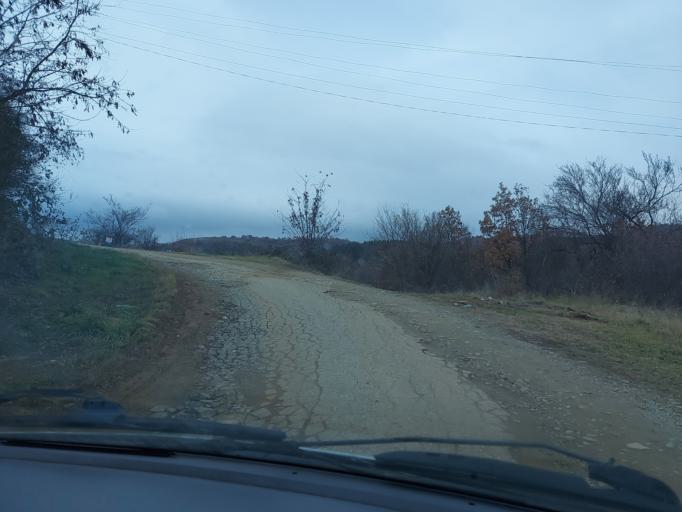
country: MK
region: Kriva Palanka
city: Kriva Palanka
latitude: 42.1884
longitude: 22.2954
